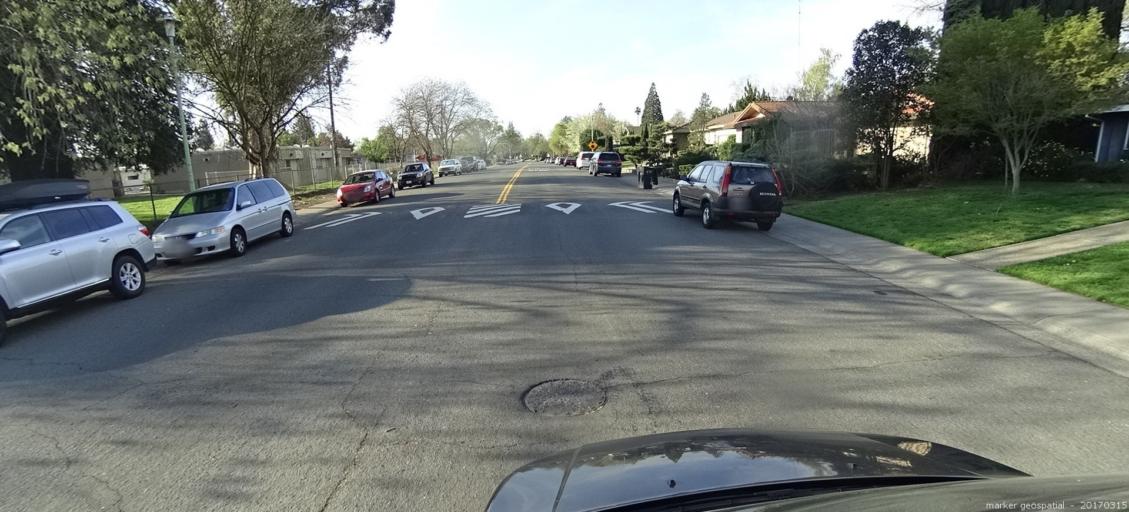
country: US
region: California
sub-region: Sacramento County
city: Parkway
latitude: 38.5141
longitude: -121.5099
